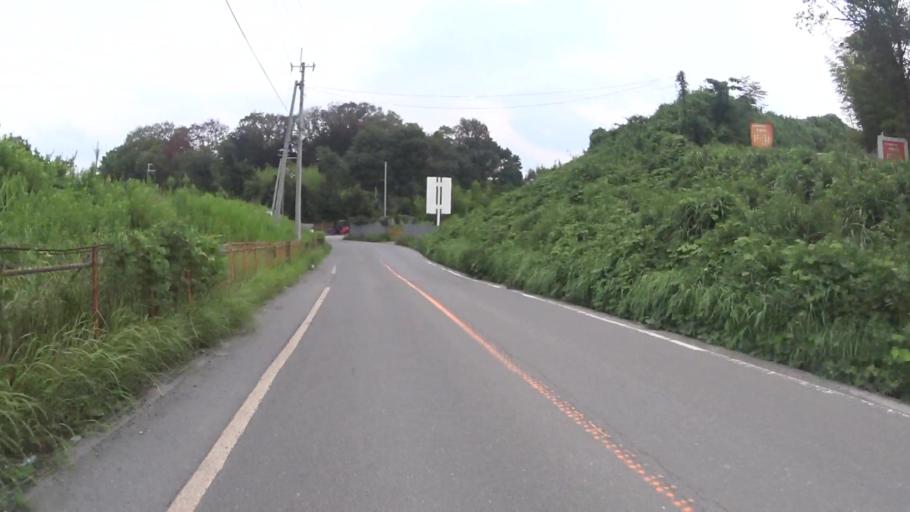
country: JP
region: Kyoto
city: Tanabe
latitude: 34.7913
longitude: 135.7449
